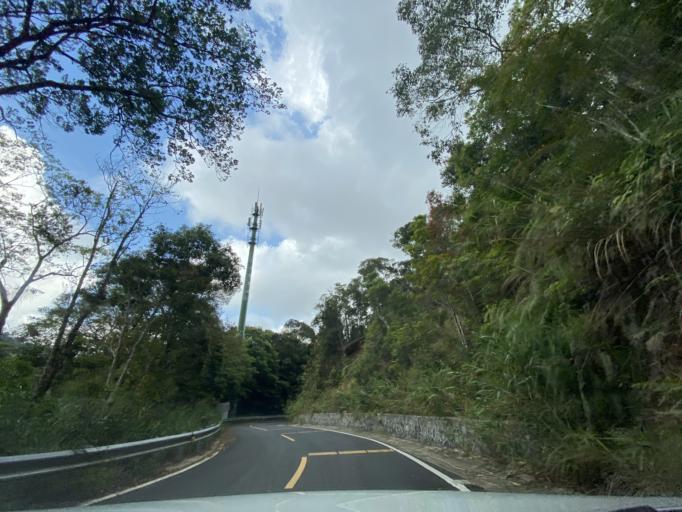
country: CN
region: Hainan
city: Diaoluoshan
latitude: 18.7079
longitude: 109.8833
